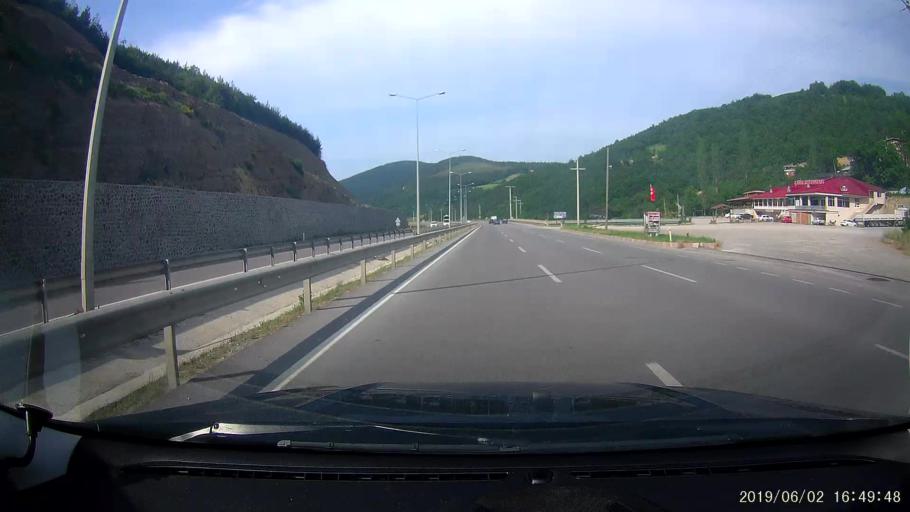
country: TR
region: Samsun
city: Samsun
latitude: 41.2423
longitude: 36.1689
